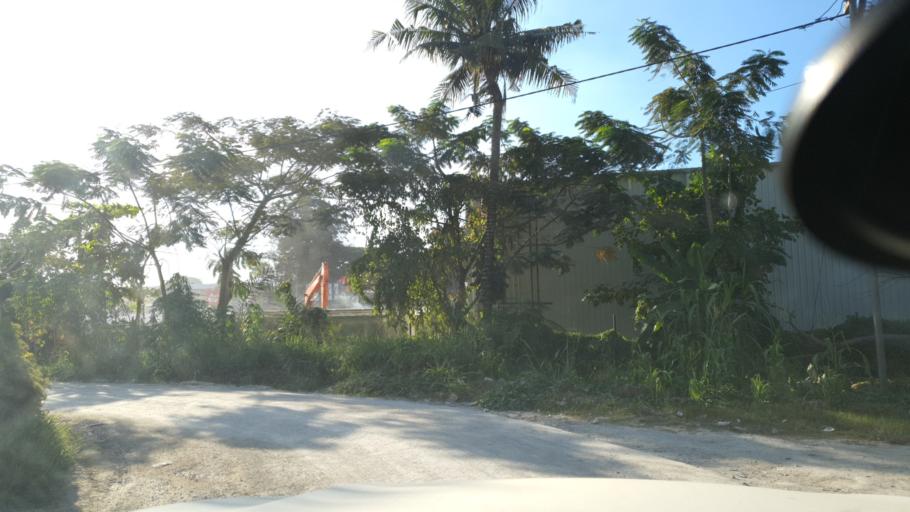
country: SB
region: Guadalcanal
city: Honiara
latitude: -9.4295
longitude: 160.0070
